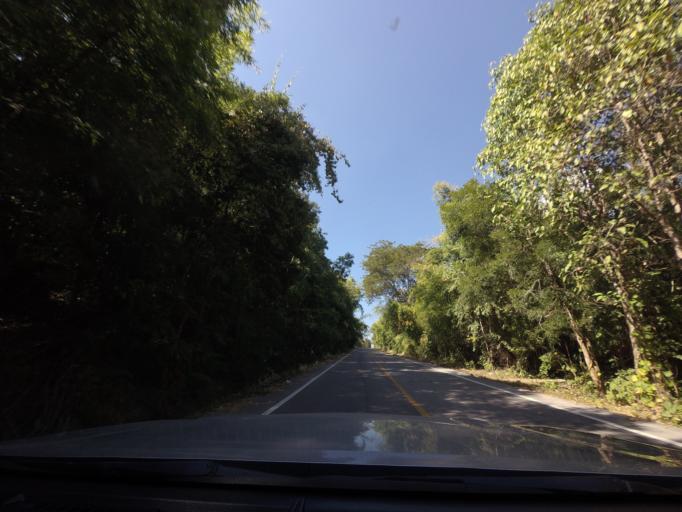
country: TH
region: Lampang
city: Chae Hom
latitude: 18.5474
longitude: 99.6354
